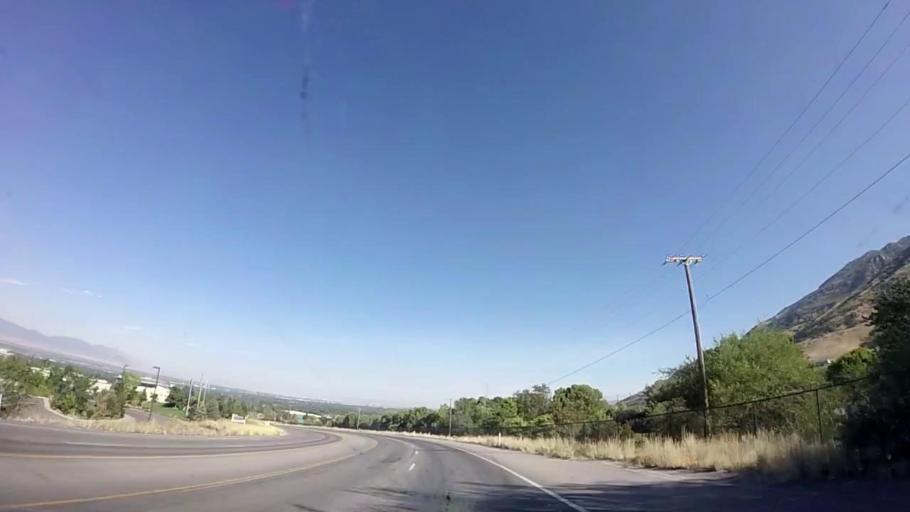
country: US
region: Utah
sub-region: Salt Lake County
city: Cottonwood Heights
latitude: 40.6342
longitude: -111.8005
